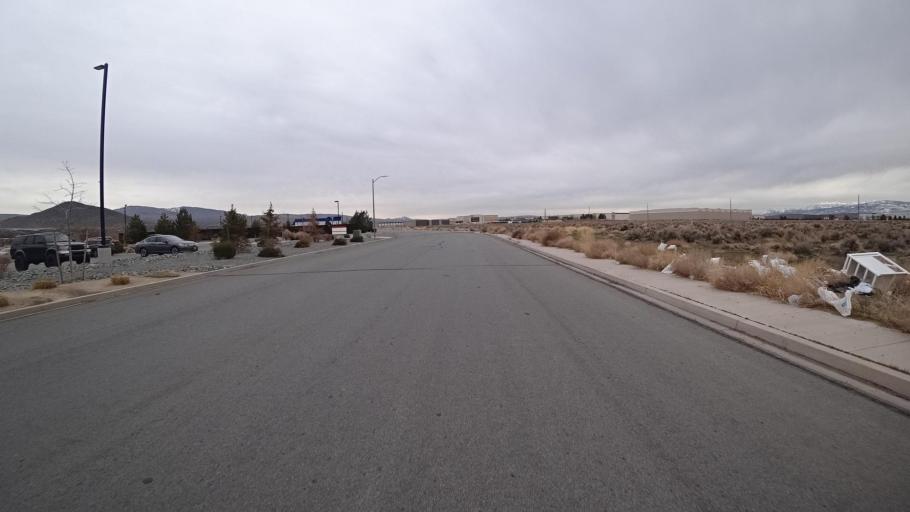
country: US
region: Nevada
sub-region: Washoe County
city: Spanish Springs
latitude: 39.6800
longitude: -119.7056
